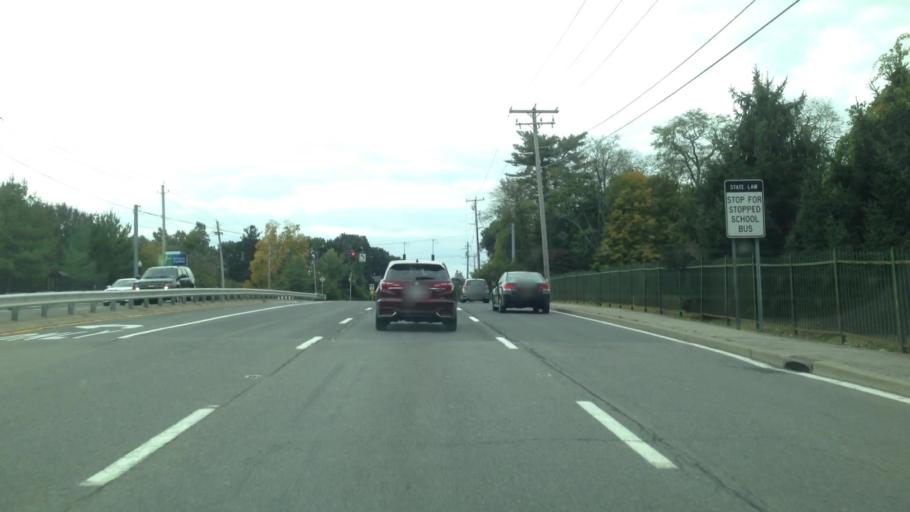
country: US
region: New York
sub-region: Dutchess County
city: Poughkeepsie
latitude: 41.6788
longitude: -73.9292
